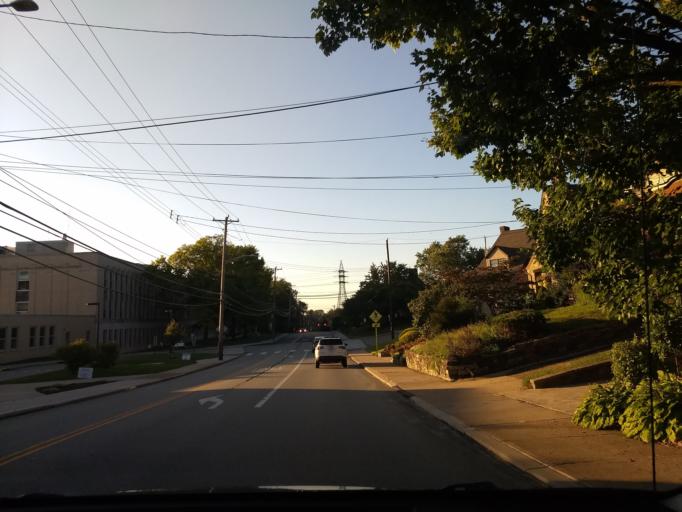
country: US
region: Pennsylvania
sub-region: Allegheny County
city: Mount Lebanon
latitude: 40.3751
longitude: -80.0498
